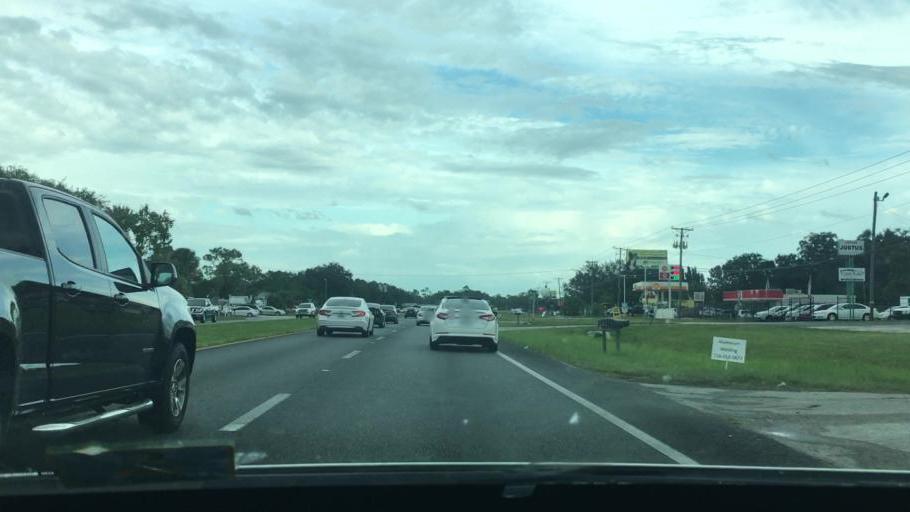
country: US
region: Florida
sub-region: Orange County
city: Bithlo
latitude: 28.5522
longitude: -81.1026
